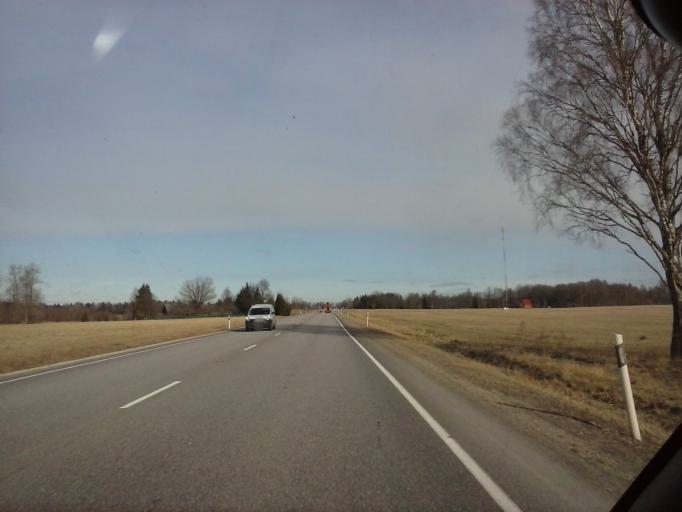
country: EE
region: Jaervamaa
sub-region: Paide linn
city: Paide
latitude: 58.8242
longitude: 25.7497
